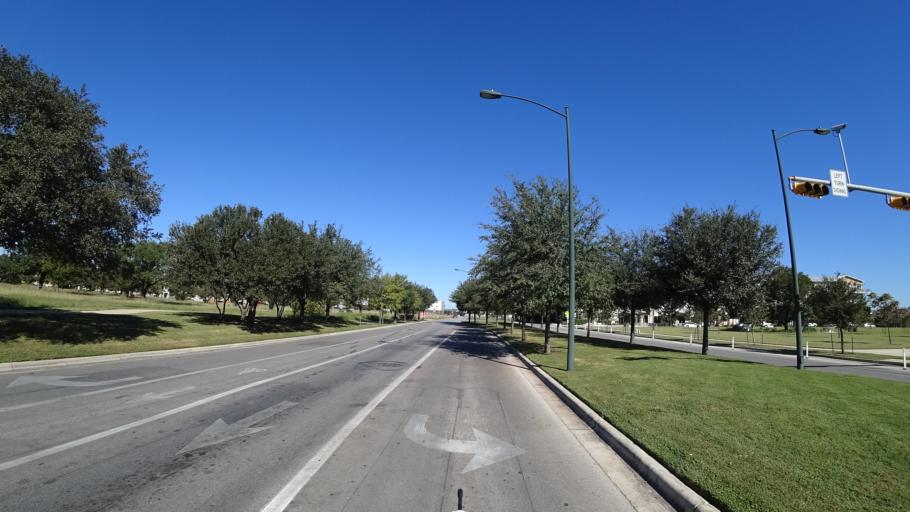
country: US
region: Texas
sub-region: Travis County
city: Austin
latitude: 30.2892
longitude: -97.6986
